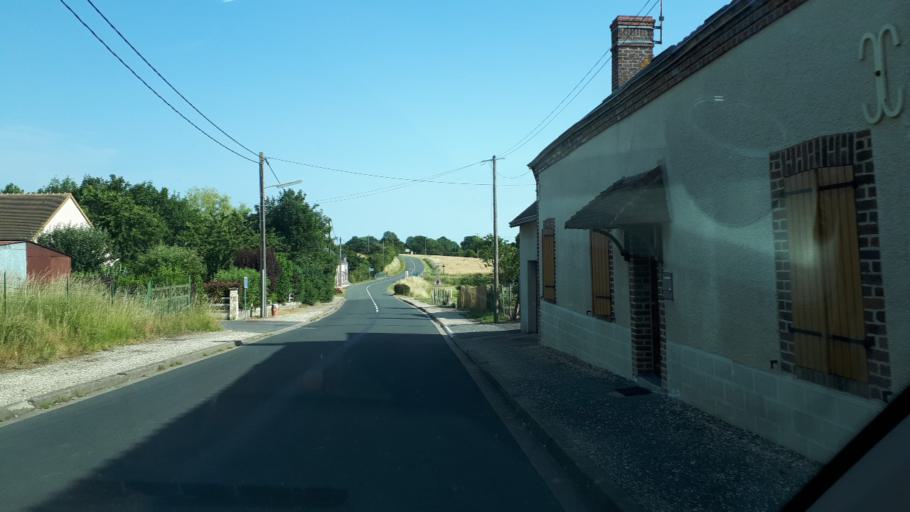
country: FR
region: Centre
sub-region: Departement du Loir-et-Cher
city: Droue
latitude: 47.9897
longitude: 1.0343
